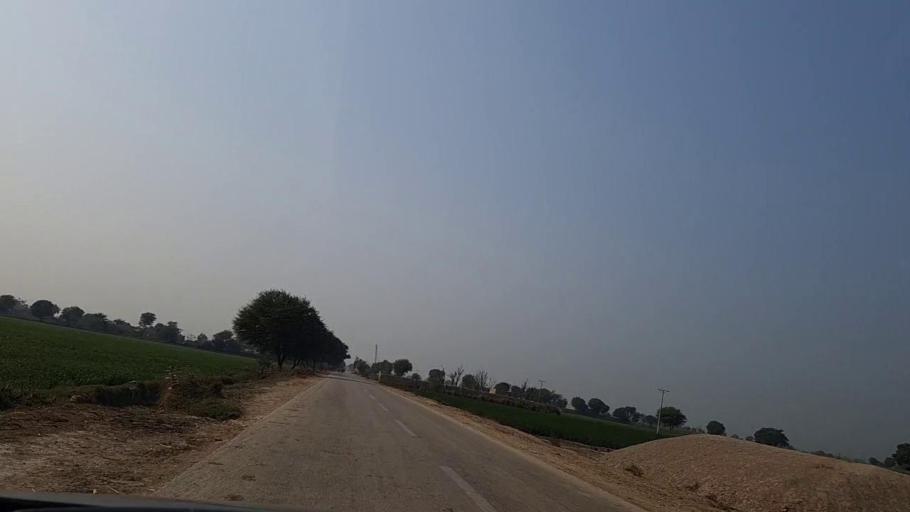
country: PK
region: Sindh
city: Sann
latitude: 26.1416
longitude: 68.1552
